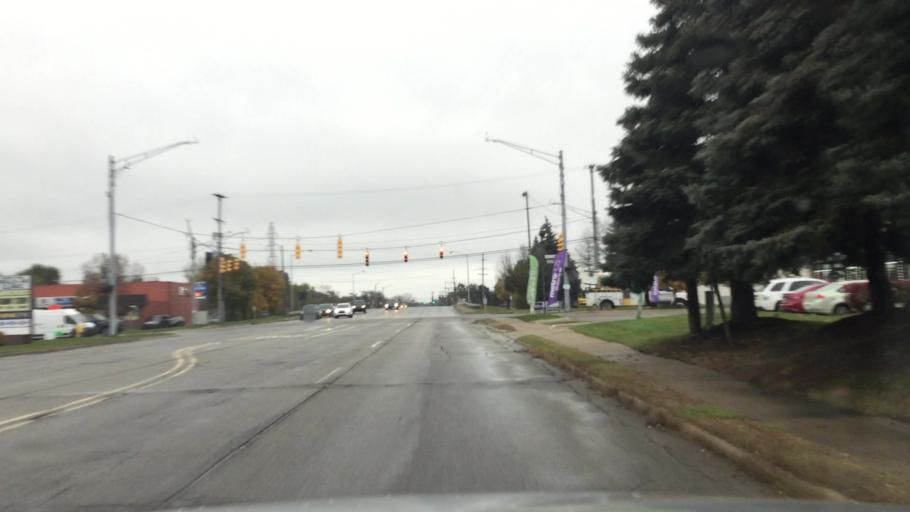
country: US
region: Michigan
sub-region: Oakland County
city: Sylvan Lake
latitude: 42.6202
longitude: -83.3195
